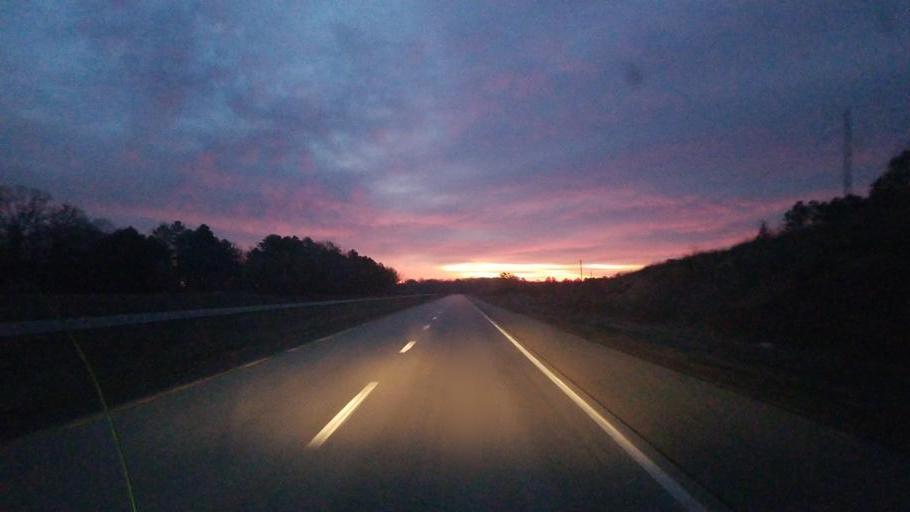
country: US
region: Missouri
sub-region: Shannon County
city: Winona
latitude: 36.9981
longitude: -91.4632
